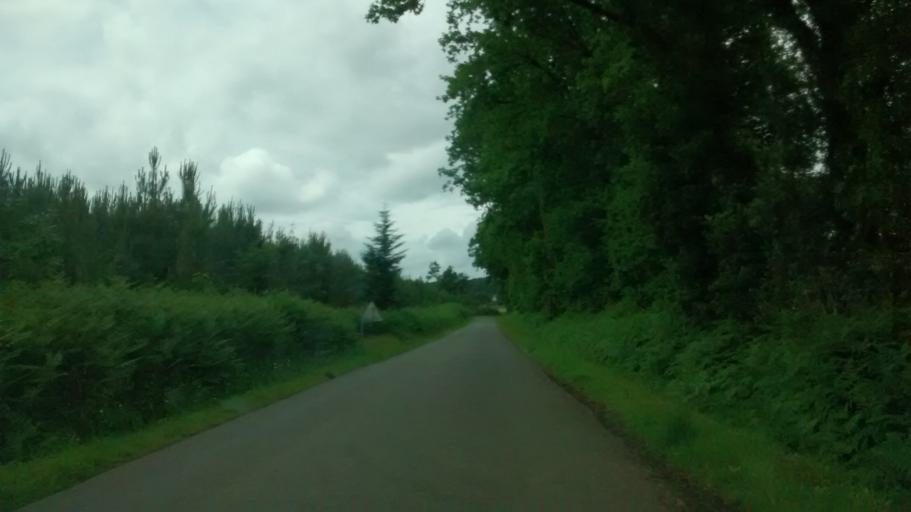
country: FR
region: Brittany
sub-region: Departement du Morbihan
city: Carentoir
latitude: 47.8348
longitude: -2.2027
